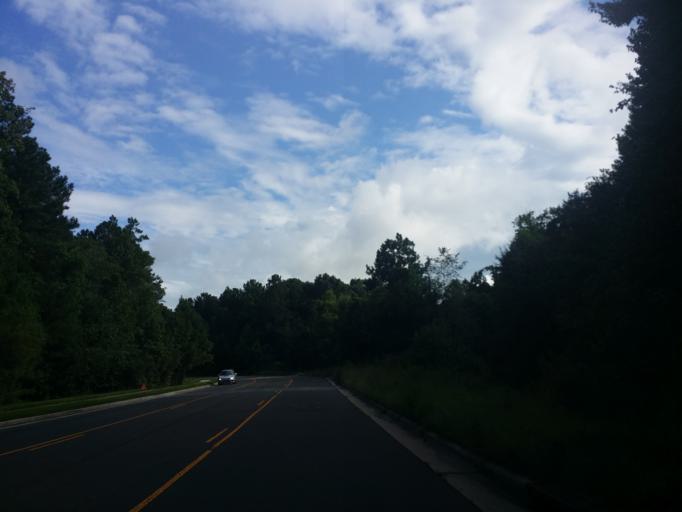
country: US
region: North Carolina
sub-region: Wake County
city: Morrisville
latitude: 35.9140
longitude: -78.7901
